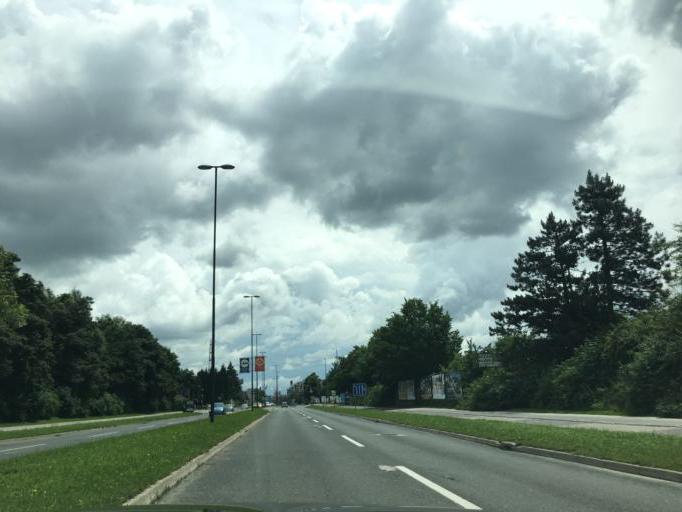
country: SI
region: Ljubljana
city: Ljubljana
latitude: 46.0918
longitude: 14.4702
